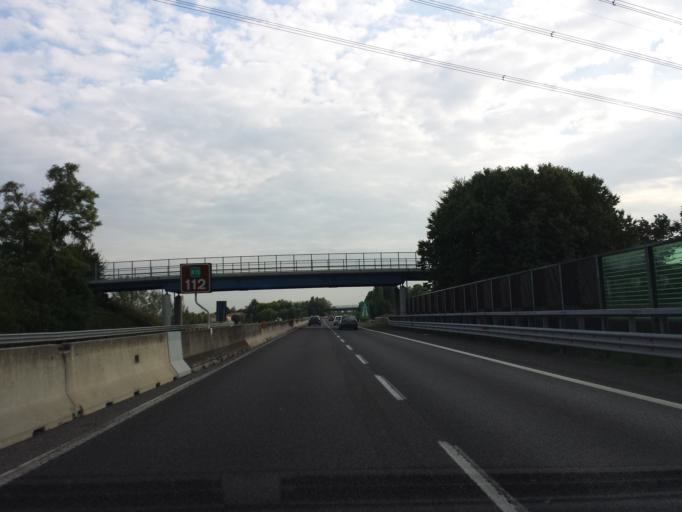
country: IT
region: Veneto
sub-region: Provincia di Padova
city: Mandriola-Sant'Agostino
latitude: 45.3605
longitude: 11.8551
